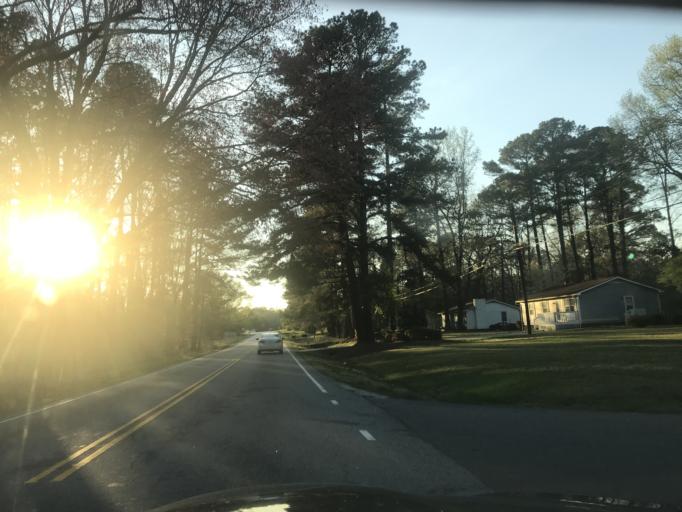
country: US
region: North Carolina
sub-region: Wake County
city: Knightdale
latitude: 35.7565
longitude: -78.5422
